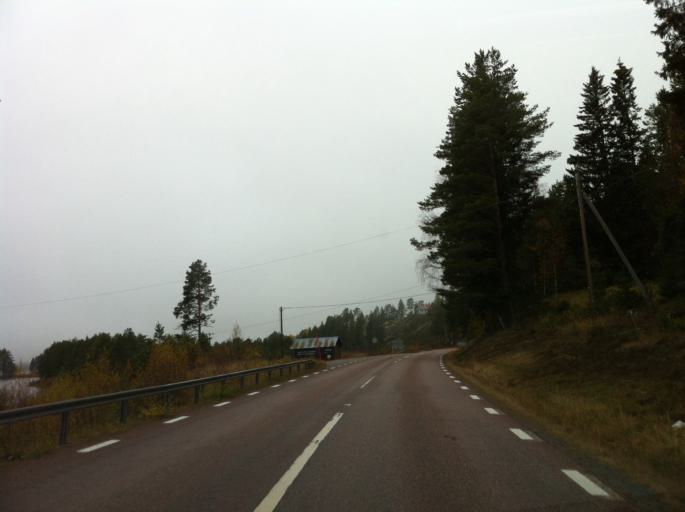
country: NO
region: Hedmark
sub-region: Trysil
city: Innbygda
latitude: 61.8539
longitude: 12.7427
